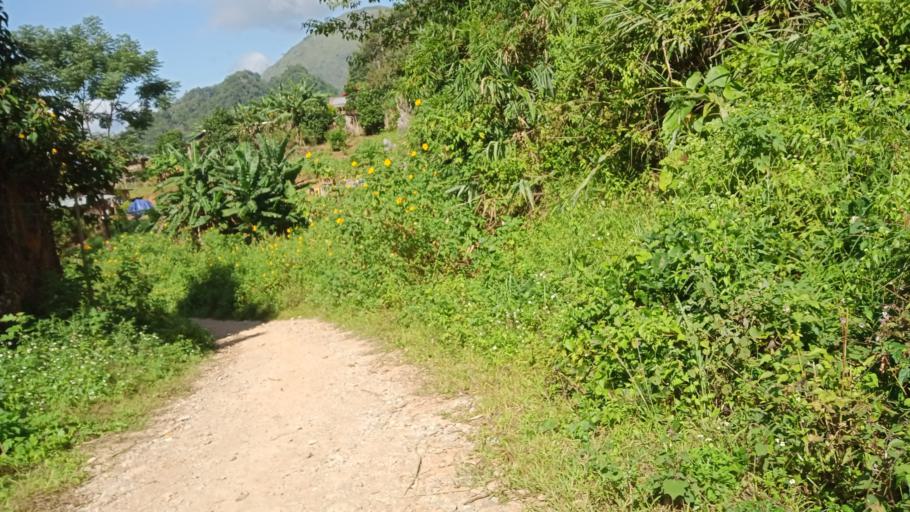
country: LA
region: Xiangkhoang
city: Phonsavan
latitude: 19.1186
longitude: 102.9133
